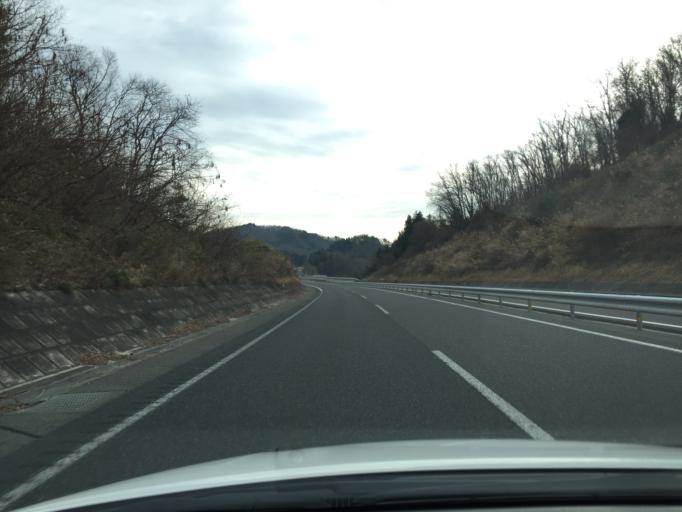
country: JP
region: Fukushima
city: Funehikimachi-funehiki
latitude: 37.4262
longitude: 140.5518
